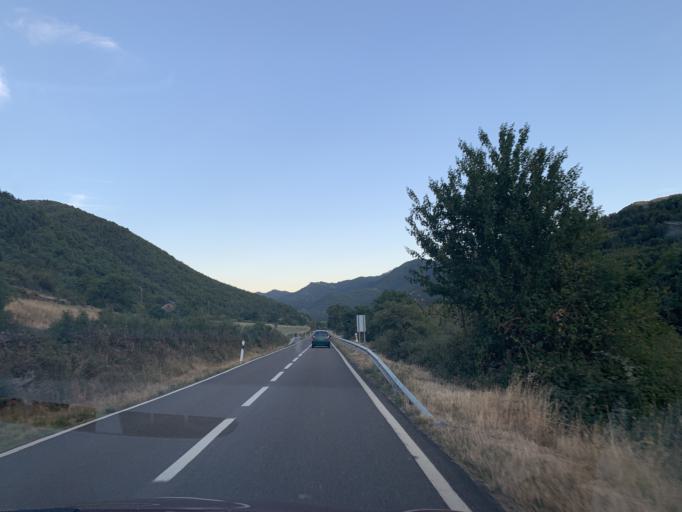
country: ES
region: Aragon
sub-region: Provincia de Huesca
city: Fiscal
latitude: 42.5081
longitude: -0.1250
